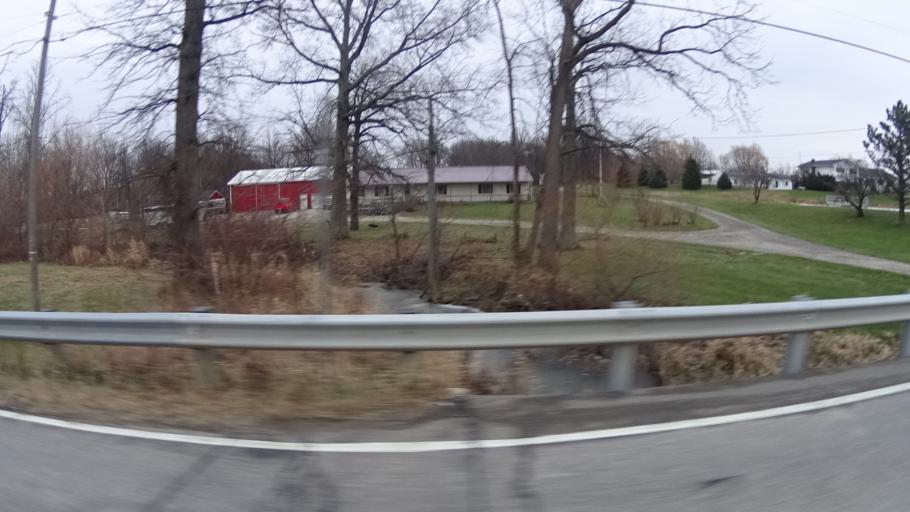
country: US
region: Ohio
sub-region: Lorain County
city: Grafton
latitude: 41.2405
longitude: -82.0425
